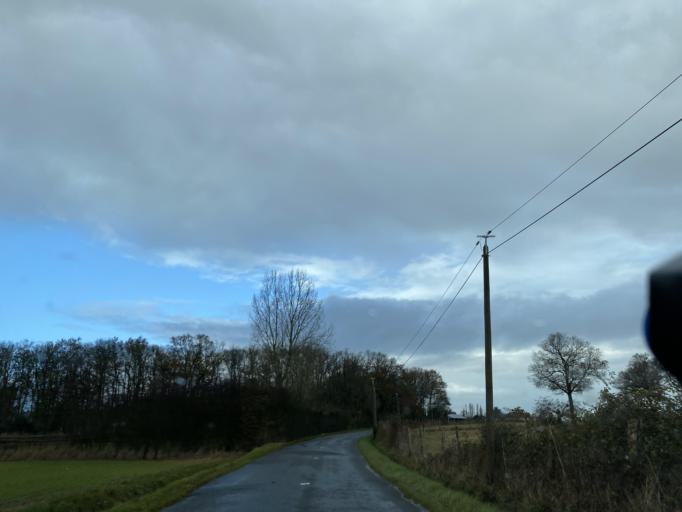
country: FR
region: Haute-Normandie
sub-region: Departement de l'Eure
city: Tillieres-sur-Avre
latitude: 48.7814
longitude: 1.0596
